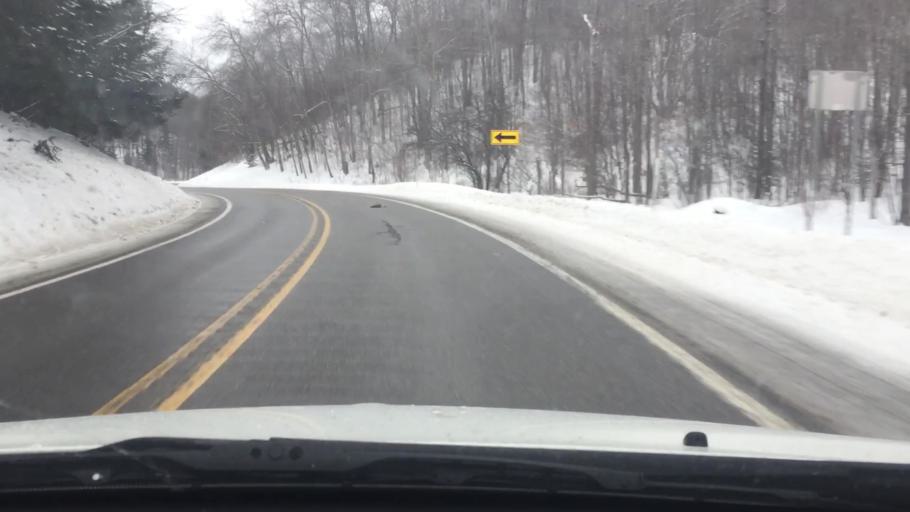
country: US
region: Michigan
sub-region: Charlevoix County
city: Boyne City
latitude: 45.0842
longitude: -84.9331
